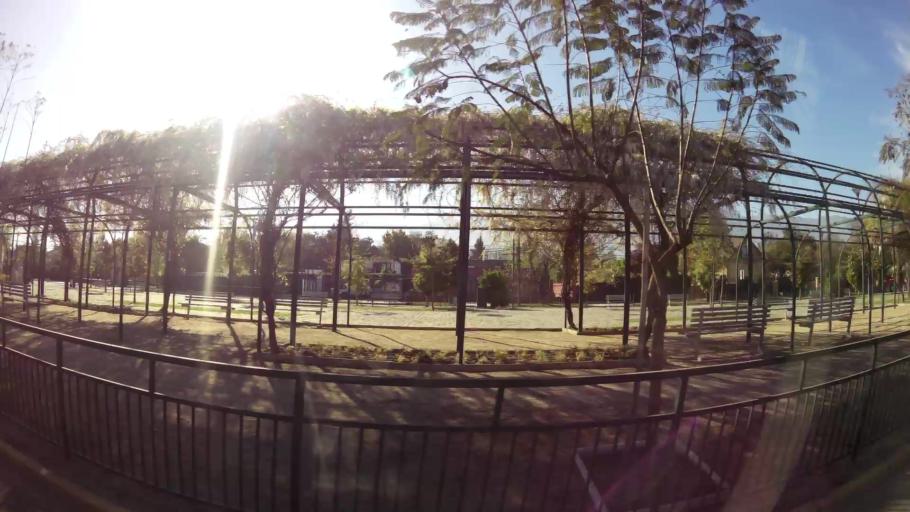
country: CL
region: Santiago Metropolitan
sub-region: Provincia de Santiago
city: Villa Presidente Frei, Nunoa, Santiago, Chile
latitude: -33.4380
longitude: -70.5564
